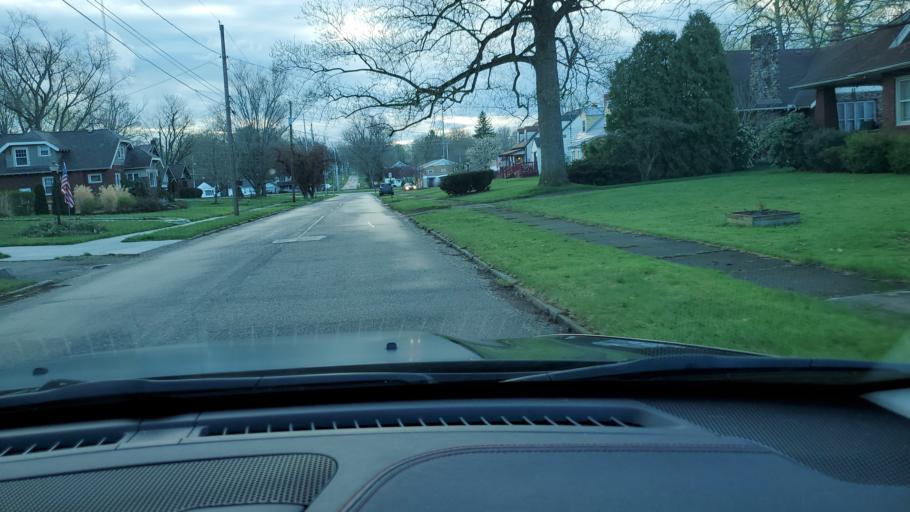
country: US
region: Ohio
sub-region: Mahoning County
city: Boardman
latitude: 41.0531
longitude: -80.6600
